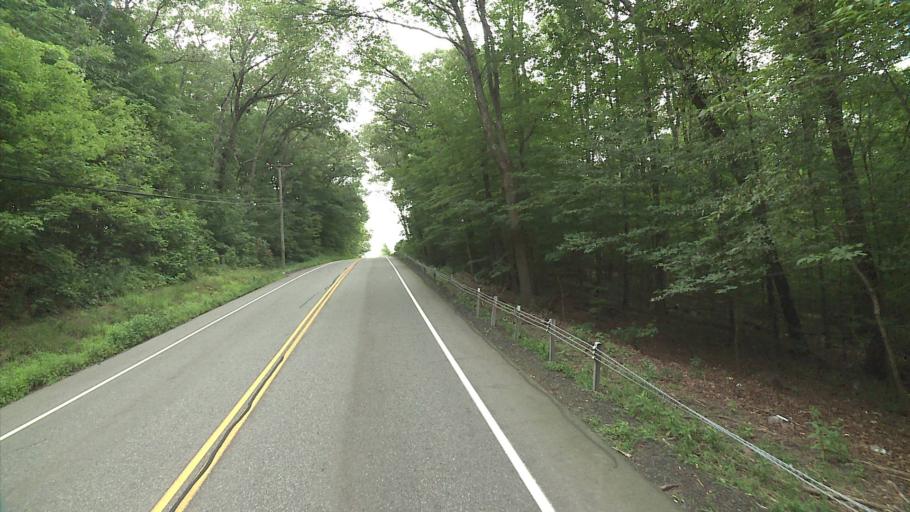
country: US
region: Connecticut
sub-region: Tolland County
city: Storrs
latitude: 41.8711
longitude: -72.2122
